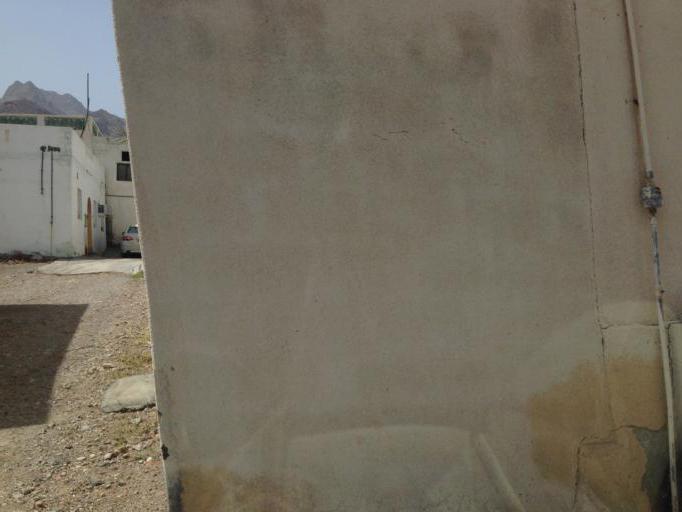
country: OM
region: Ash Sharqiyah
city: Ibra'
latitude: 23.0882
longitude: 58.8542
